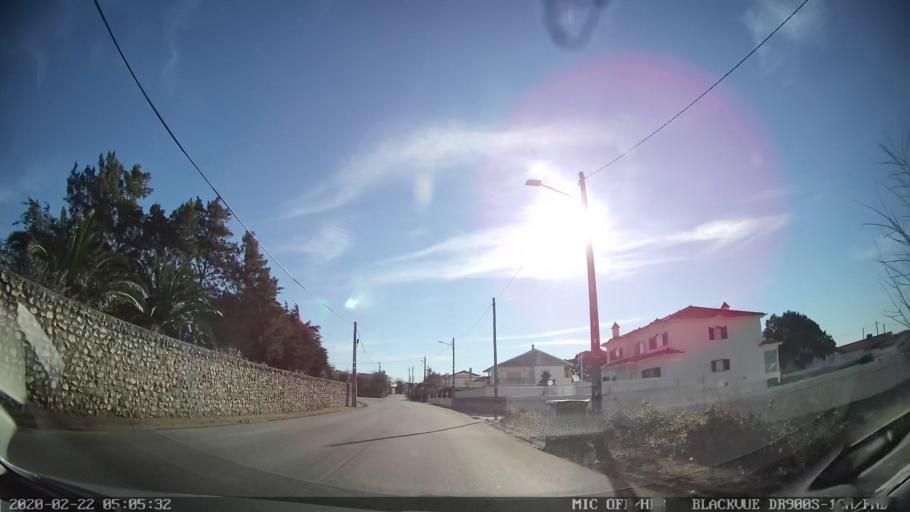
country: PT
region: Lisbon
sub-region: Vila Franca de Xira
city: Vila Franca de Xira
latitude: 38.9717
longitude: -9.0080
